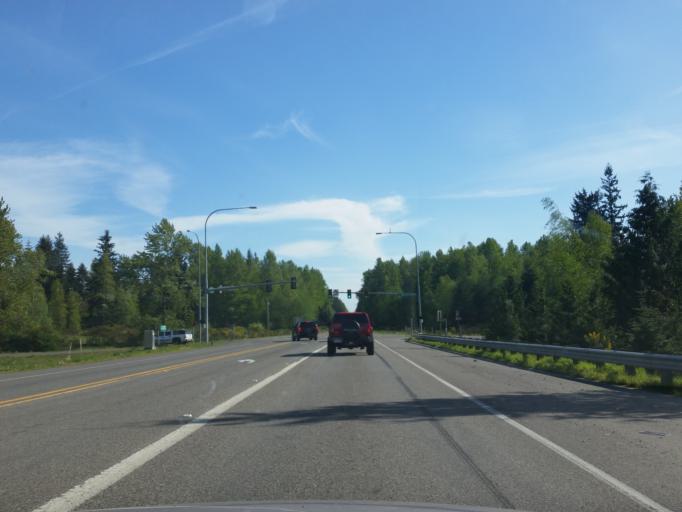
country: US
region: Washington
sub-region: Snohomish County
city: Fobes Hill
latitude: 47.9515
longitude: -122.1014
